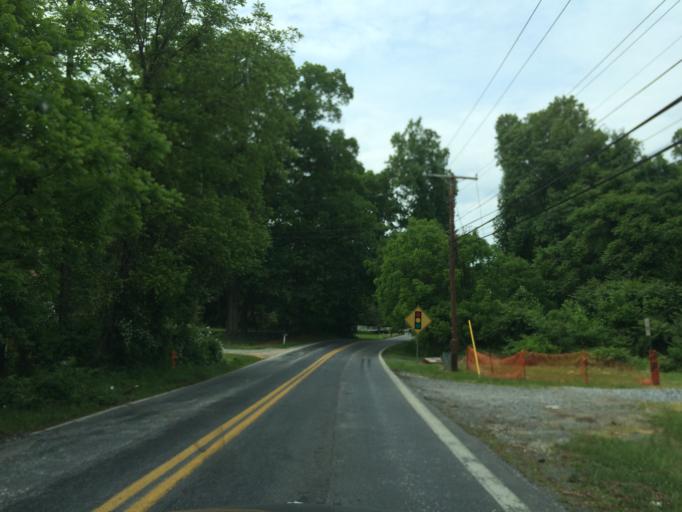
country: US
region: Maryland
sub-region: Howard County
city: Columbia
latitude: 39.2935
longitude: -76.9020
